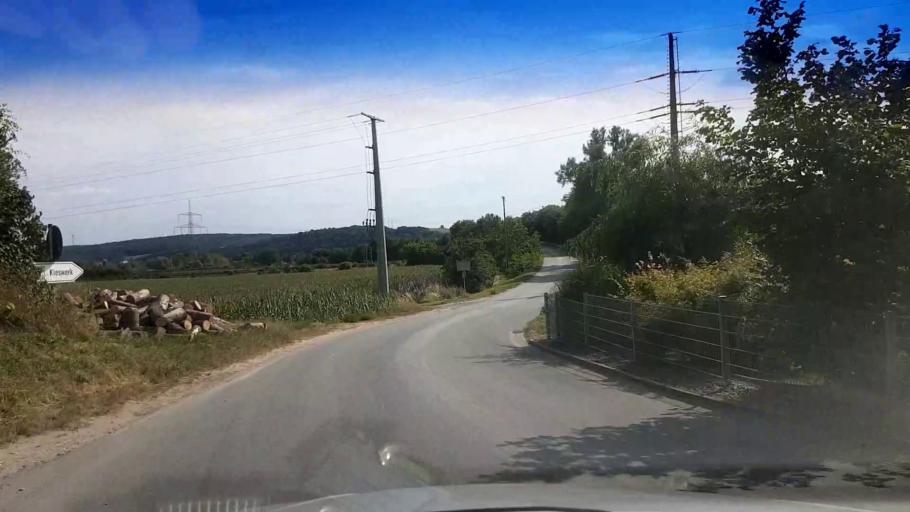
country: DE
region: Bavaria
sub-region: Regierungsbezirk Unterfranken
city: Stettfeld
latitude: 49.9687
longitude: 10.7227
